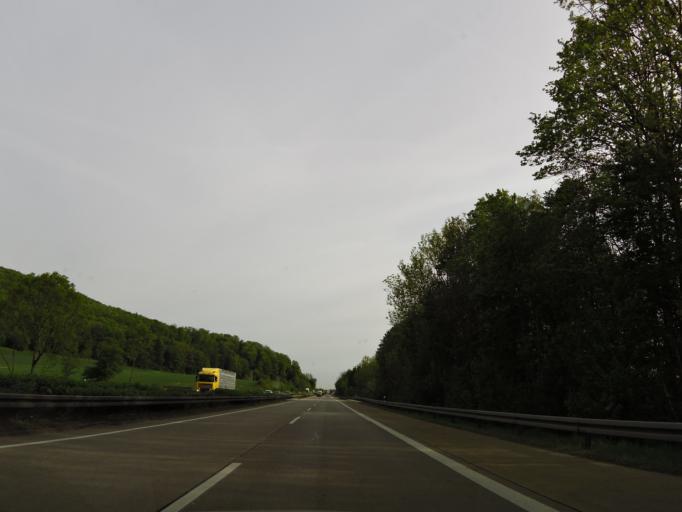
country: DE
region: Lower Saxony
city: Seesen
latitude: 51.8661
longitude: 10.1264
